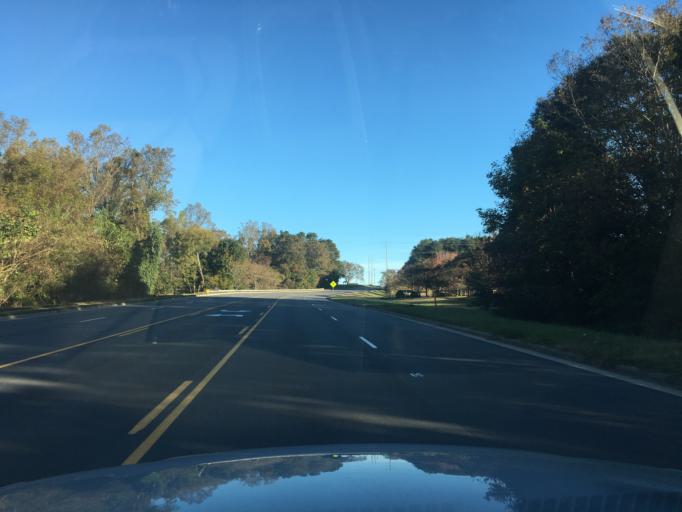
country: US
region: North Carolina
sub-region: Catawba County
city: Hickory
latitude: 35.7109
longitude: -81.3448
